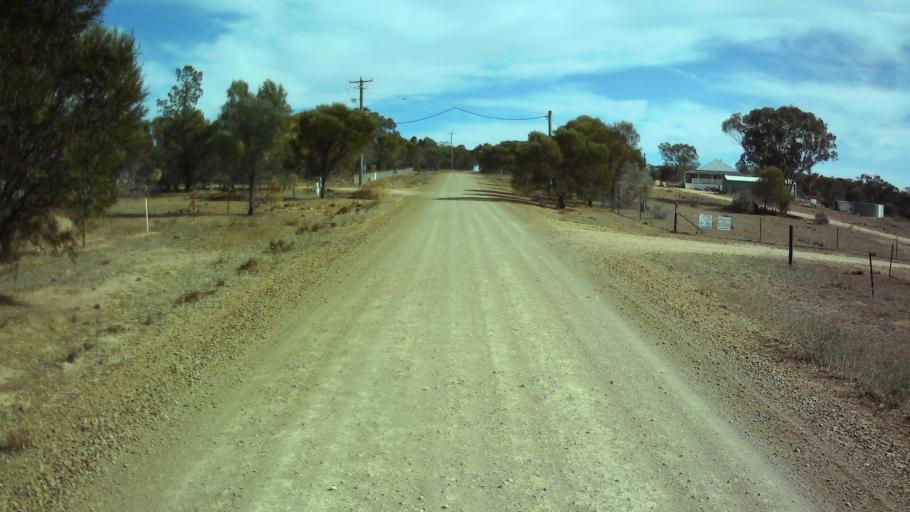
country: AU
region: New South Wales
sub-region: Weddin
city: Grenfell
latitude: -33.8741
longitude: 148.1925
